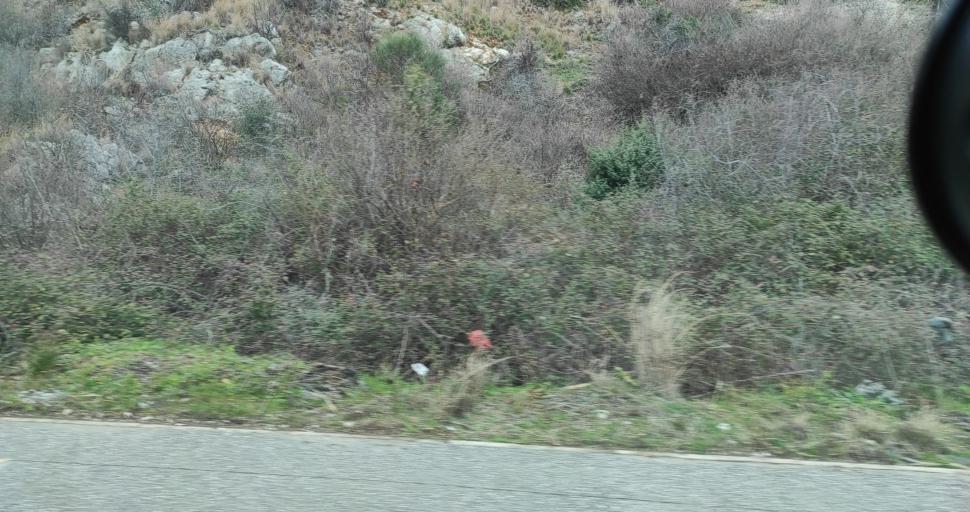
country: AL
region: Lezhe
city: Shengjin
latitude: 41.8005
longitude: 19.6166
